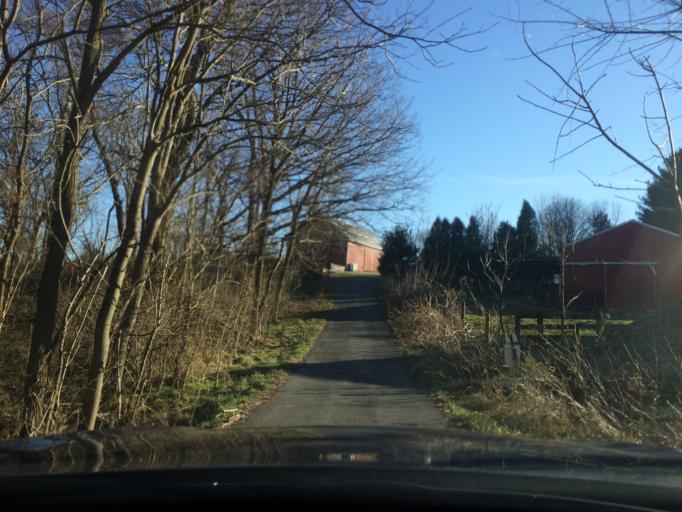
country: US
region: Maryland
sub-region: Carroll County
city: Eldersburg
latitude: 39.4475
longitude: -76.9797
